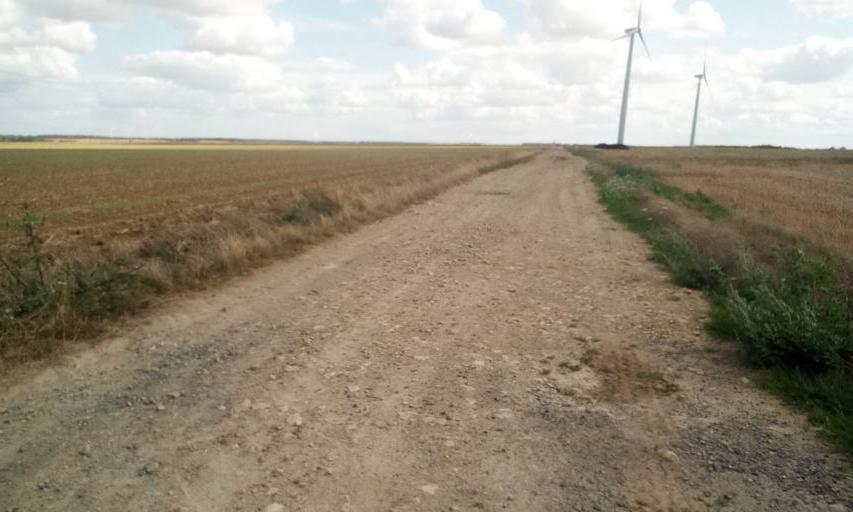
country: FR
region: Lower Normandy
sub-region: Departement du Calvados
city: Bellengreville
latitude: 49.0991
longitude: -0.2290
